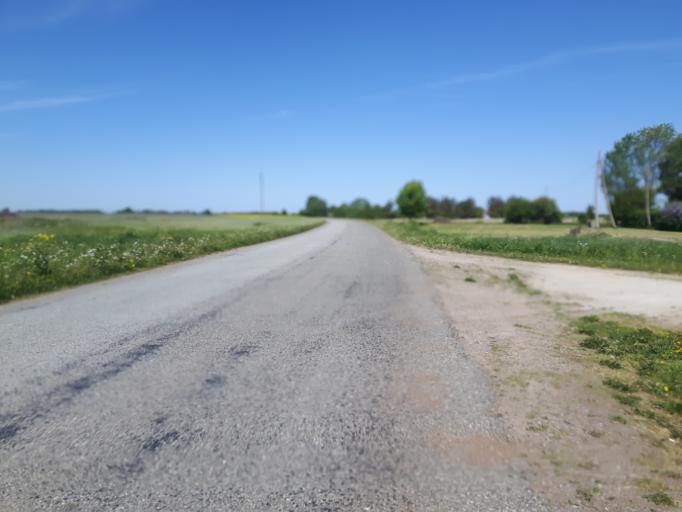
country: EE
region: Ida-Virumaa
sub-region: Aseri vald
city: Aseri
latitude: 59.4683
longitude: 26.8189
